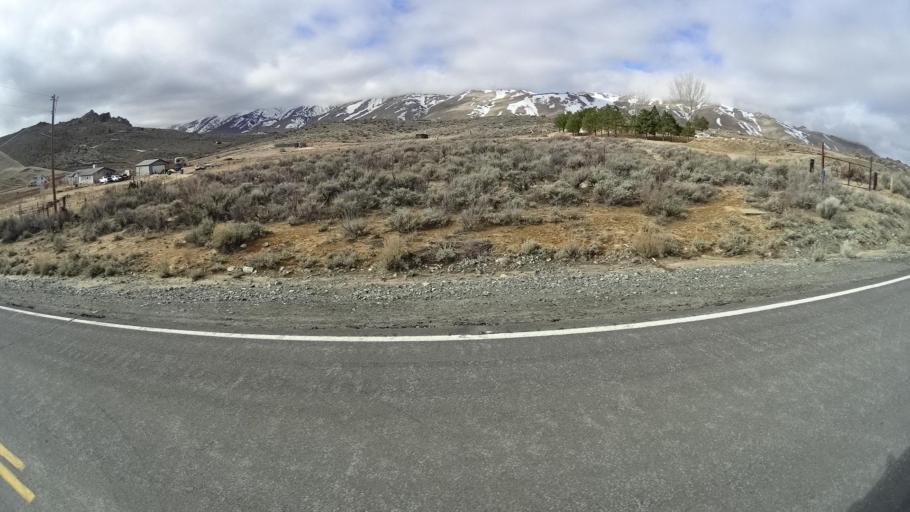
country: US
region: Nevada
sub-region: Washoe County
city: Cold Springs
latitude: 39.8665
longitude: -119.9449
